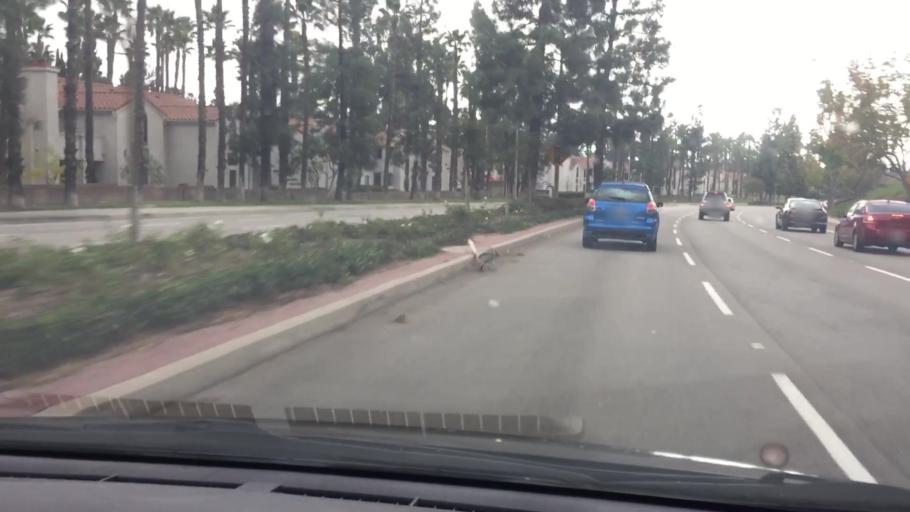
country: US
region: California
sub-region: Orange County
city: Mission Viejo
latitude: 33.6175
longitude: -117.6757
